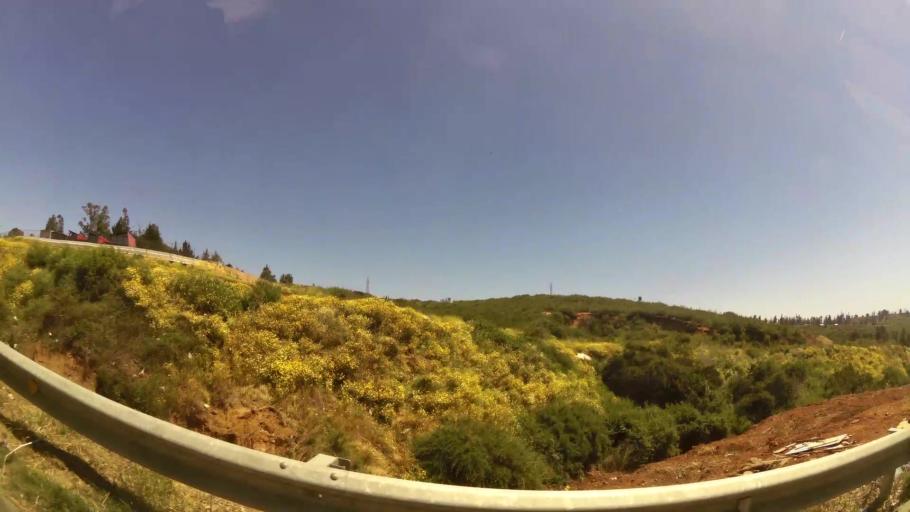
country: CL
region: Valparaiso
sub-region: Provincia de Valparaiso
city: Valparaiso
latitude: -33.0618
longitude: -71.6378
